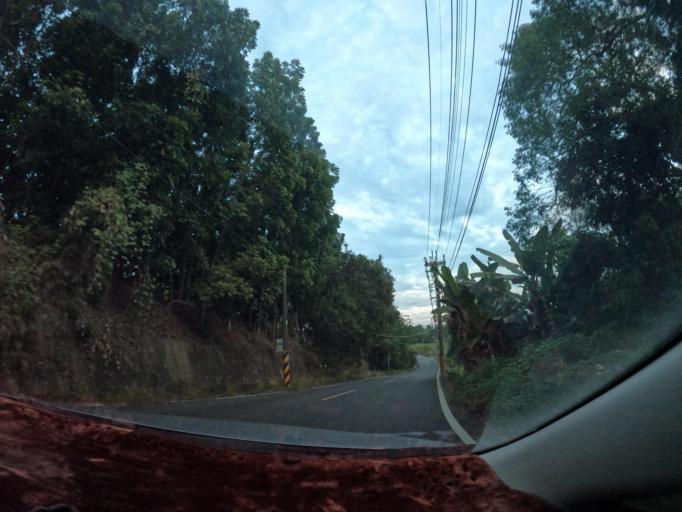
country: TW
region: Taiwan
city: Yujing
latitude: 23.0345
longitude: 120.4155
